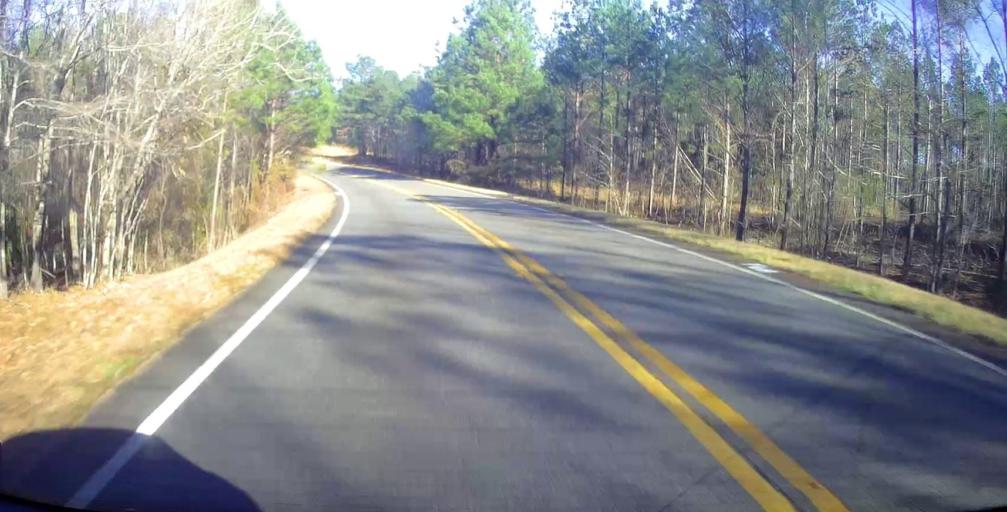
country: US
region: Georgia
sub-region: Talbot County
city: Sardis
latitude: 32.7778
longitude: -84.6699
